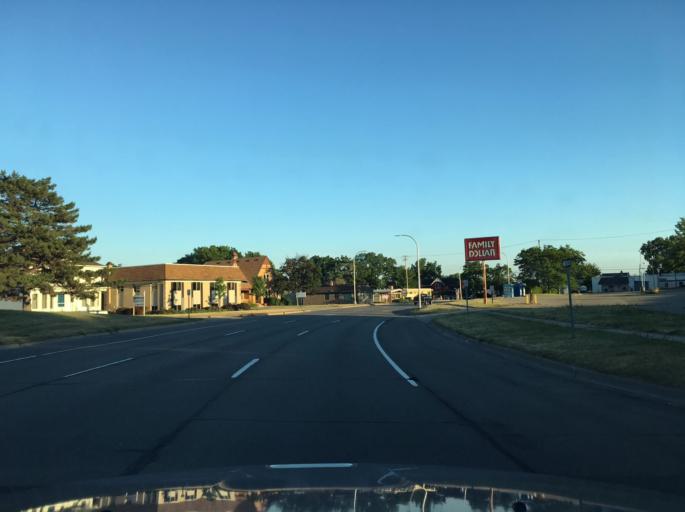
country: US
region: Michigan
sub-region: Macomb County
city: Mount Clemens
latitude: 42.5892
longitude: -82.8822
